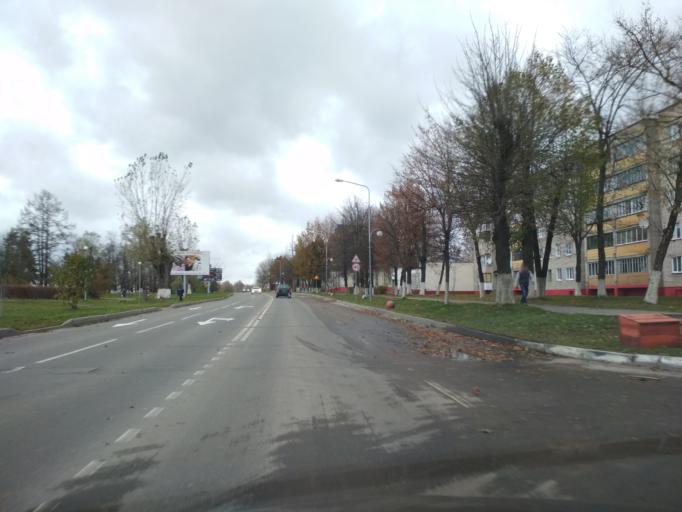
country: BY
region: Minsk
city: Mar''ina Horka
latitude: 53.5139
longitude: 28.1422
